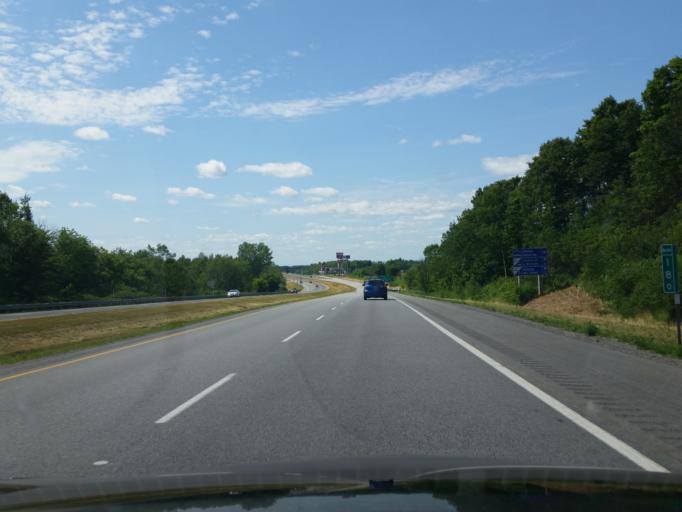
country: CA
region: Quebec
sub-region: Monteregie
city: Hudson
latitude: 45.4548
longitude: -74.2168
